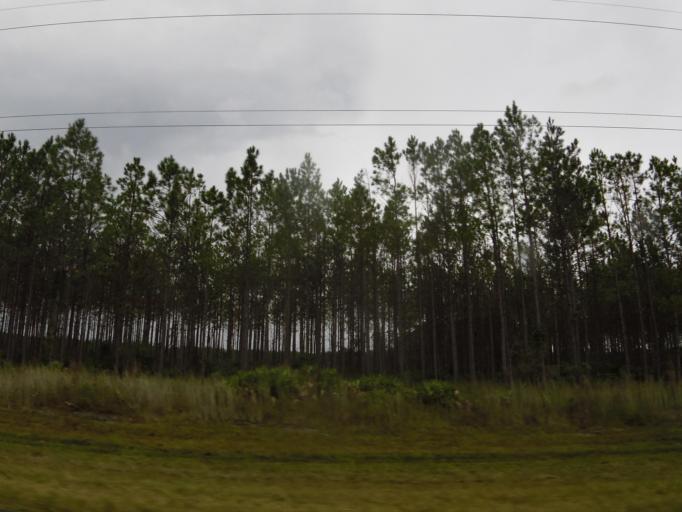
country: US
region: Florida
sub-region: Duval County
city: Baldwin
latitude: 30.4735
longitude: -82.0523
